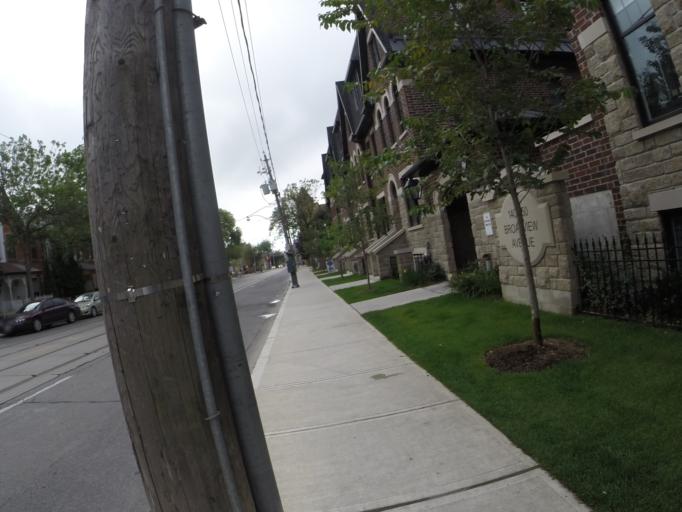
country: CA
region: Ontario
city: Toronto
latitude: 43.6615
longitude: -79.3510
